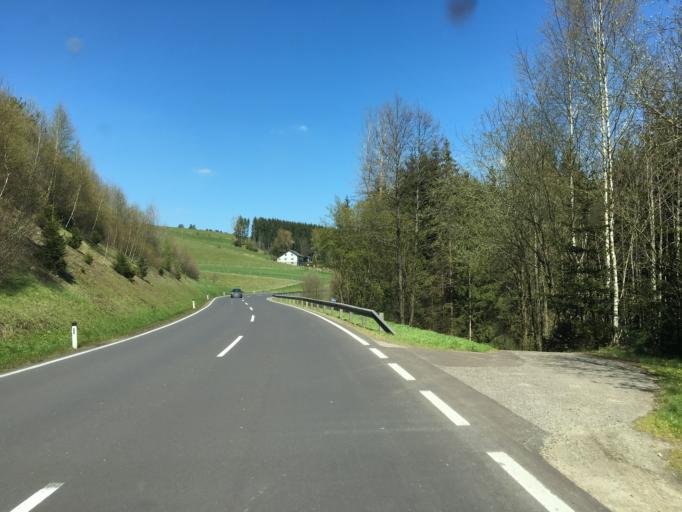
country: AT
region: Upper Austria
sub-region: Politischer Bezirk Urfahr-Umgebung
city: Zwettl an der Rodl
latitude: 48.4721
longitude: 14.2811
